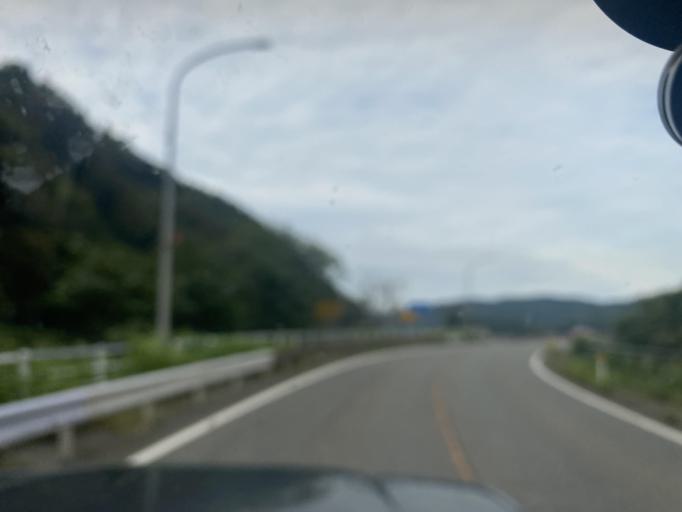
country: JP
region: Niigata
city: Itoigawa
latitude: 36.9869
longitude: 137.8670
